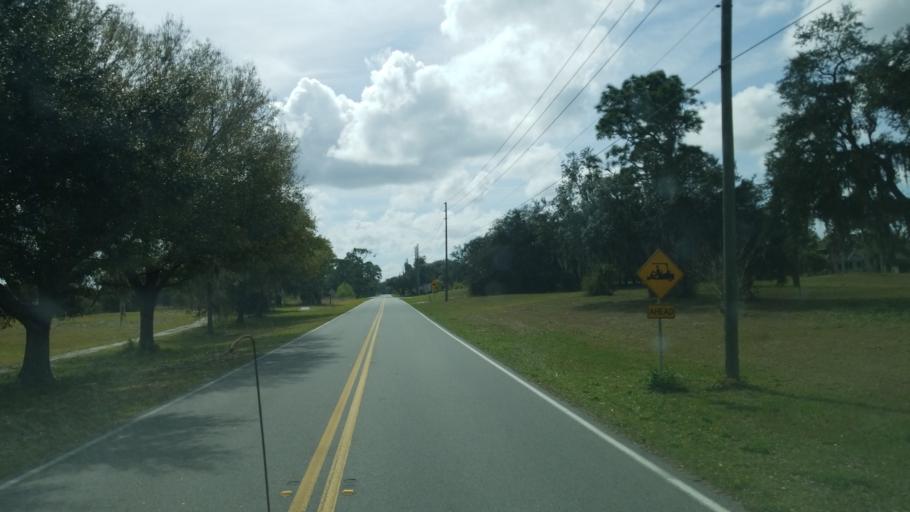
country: US
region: Florida
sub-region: Polk County
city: Dundee
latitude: 28.0188
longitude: -81.5292
